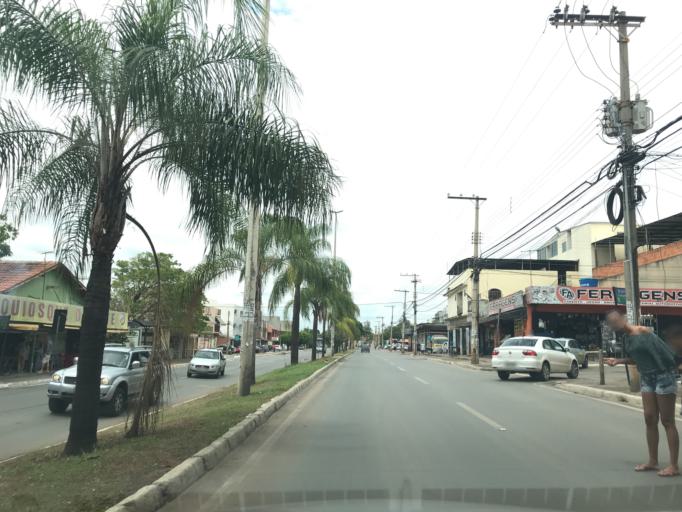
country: BR
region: Federal District
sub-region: Brasilia
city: Brasilia
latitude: -15.8562
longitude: -47.9528
